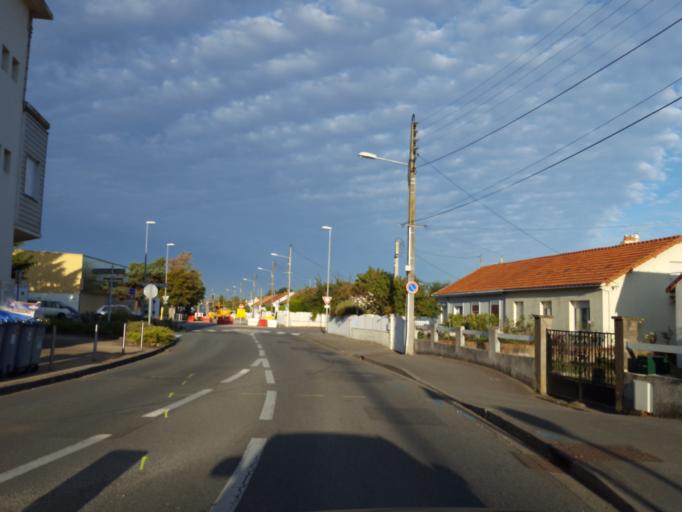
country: FR
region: Pays de la Loire
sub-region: Departement de la Loire-Atlantique
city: Saint-Sebastien-sur-Loire
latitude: 47.1959
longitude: -1.4874
